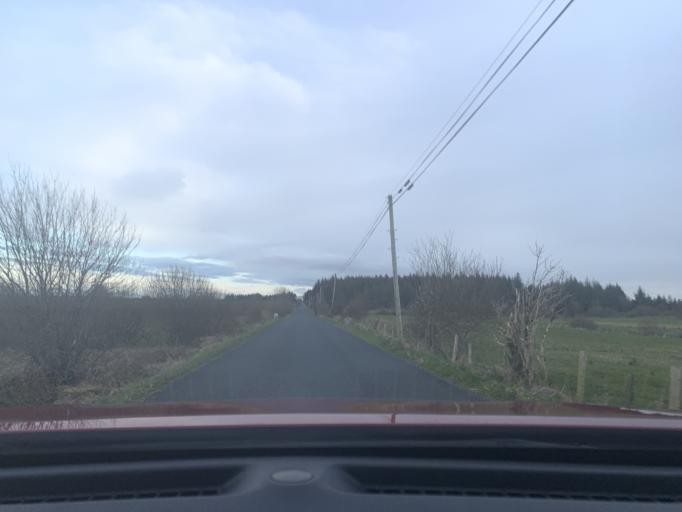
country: IE
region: Connaught
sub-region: Roscommon
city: Ballaghaderreen
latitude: 53.8875
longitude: -8.5696
